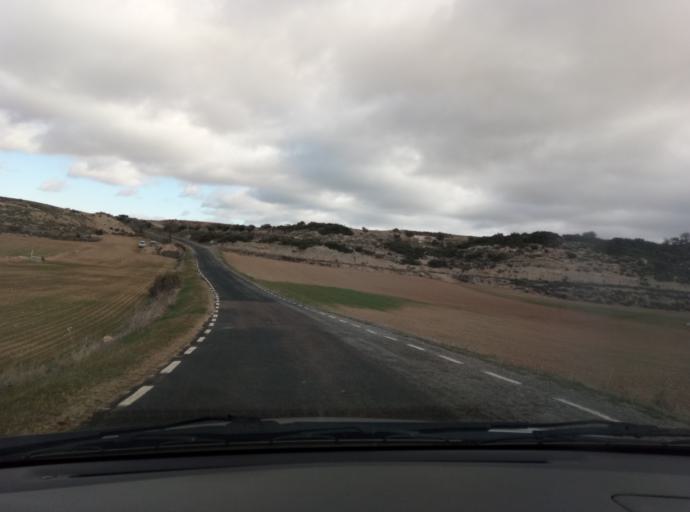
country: ES
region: Catalonia
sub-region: Provincia de Lleida
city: Nalec
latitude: 41.5864
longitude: 1.0843
